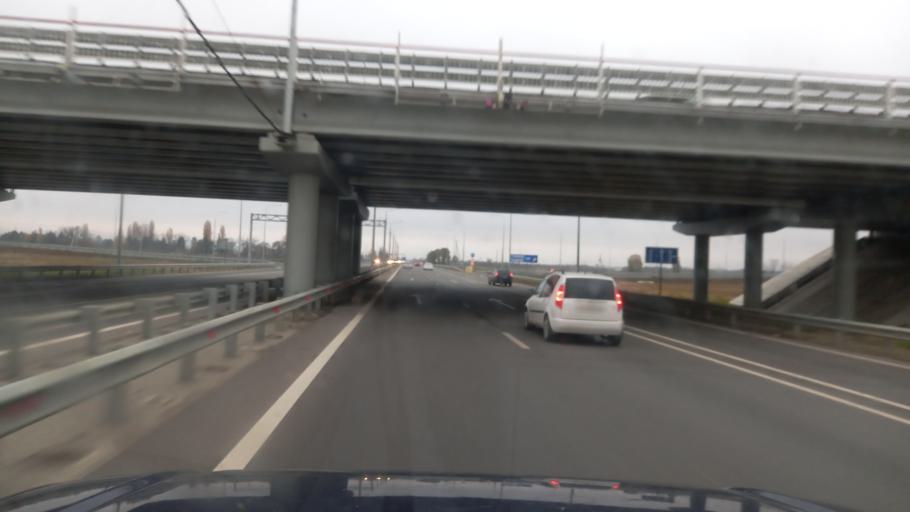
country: RU
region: Adygeya
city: Maykop
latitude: 44.6302
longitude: 40.0433
